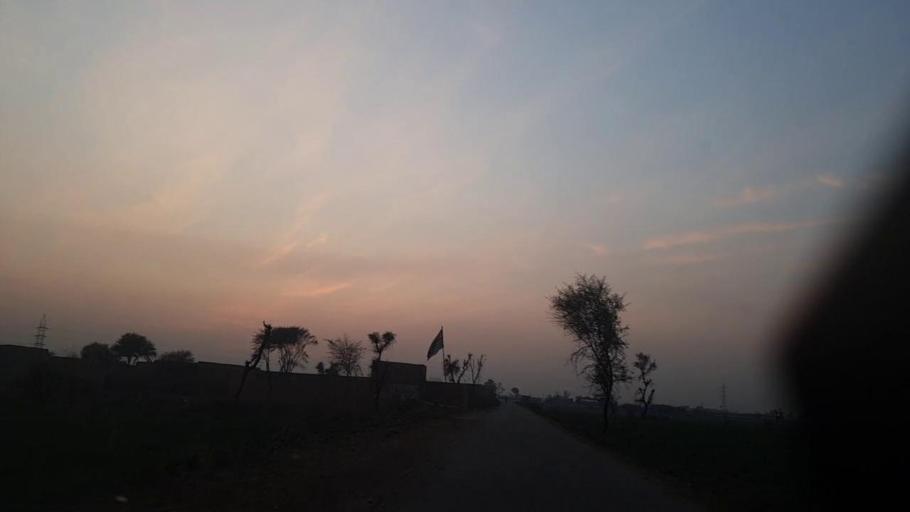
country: PK
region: Sindh
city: Sakrand
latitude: 26.1019
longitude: 68.3013
